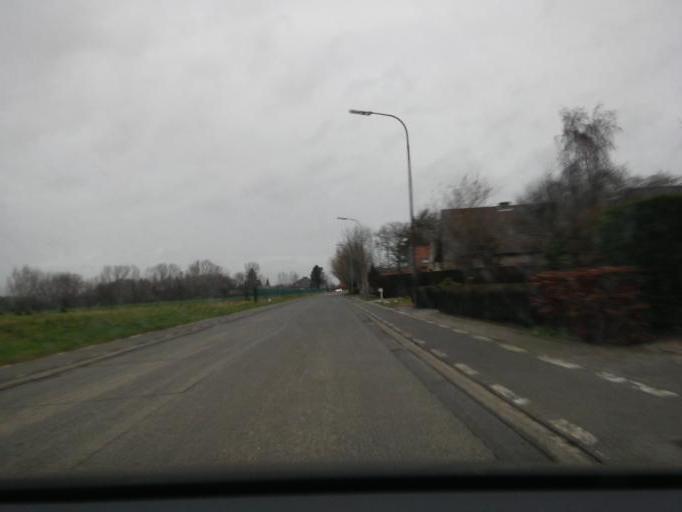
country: BE
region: Flanders
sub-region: Provincie Oost-Vlaanderen
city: Wetteren
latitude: 51.0298
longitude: 3.8913
